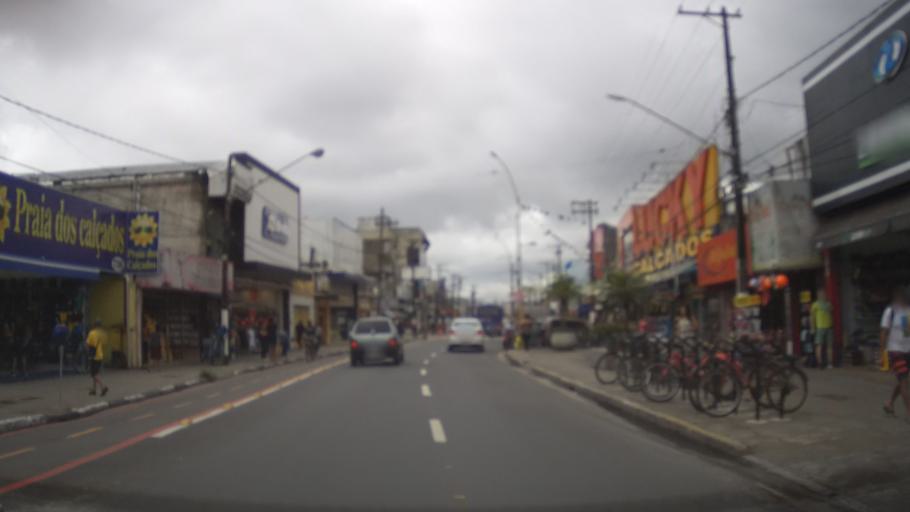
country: BR
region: Sao Paulo
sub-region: Santos
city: Santos
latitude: -23.9428
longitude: -46.3016
